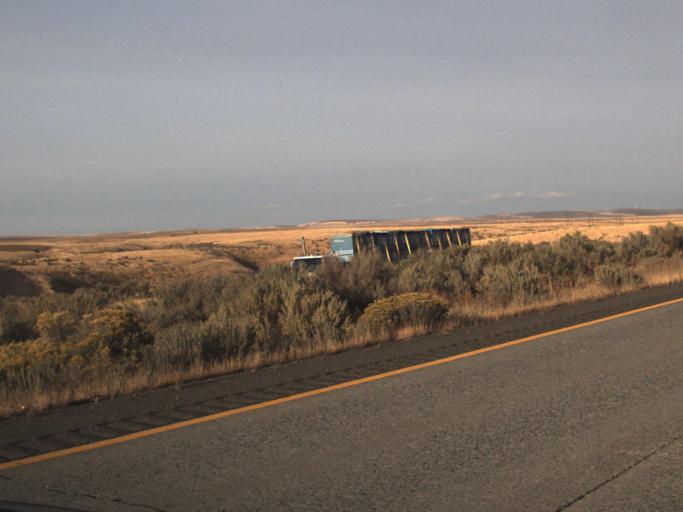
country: US
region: Oregon
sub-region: Umatilla County
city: Umatilla
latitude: 45.9941
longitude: -119.2817
